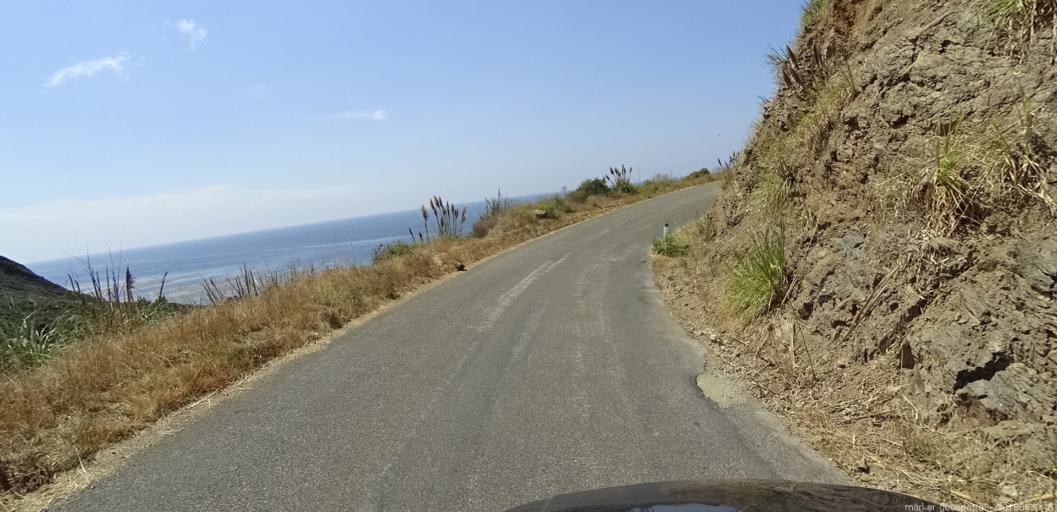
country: US
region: California
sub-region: Monterey County
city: Greenfield
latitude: 35.9849
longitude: -121.4892
